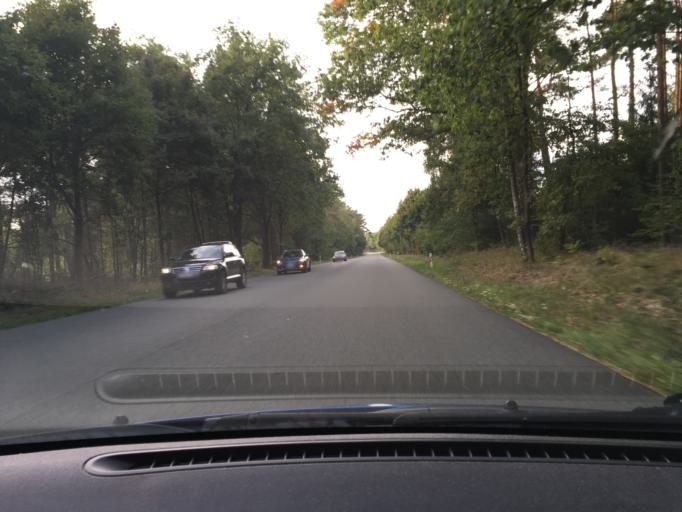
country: DE
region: Lower Saxony
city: Munster
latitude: 52.9140
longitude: 10.0817
